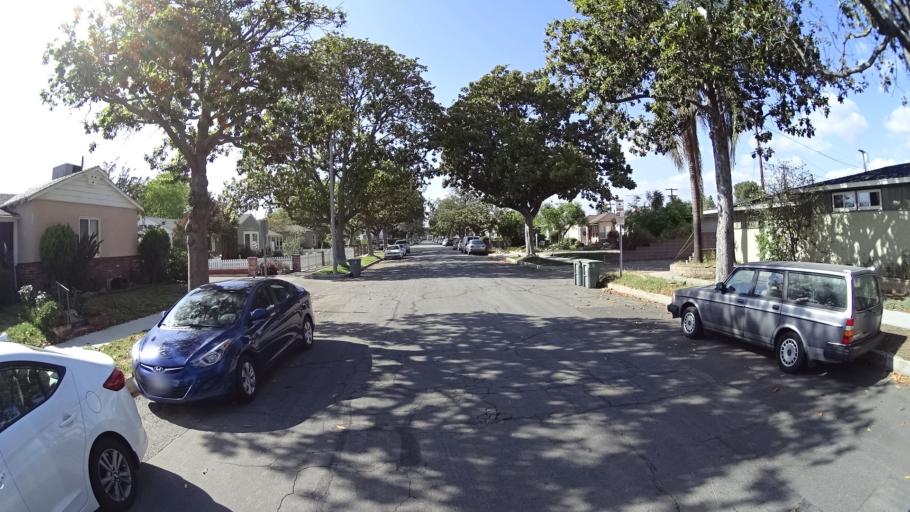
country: US
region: California
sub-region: Los Angeles County
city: North Hollywood
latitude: 34.1703
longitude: -118.3525
